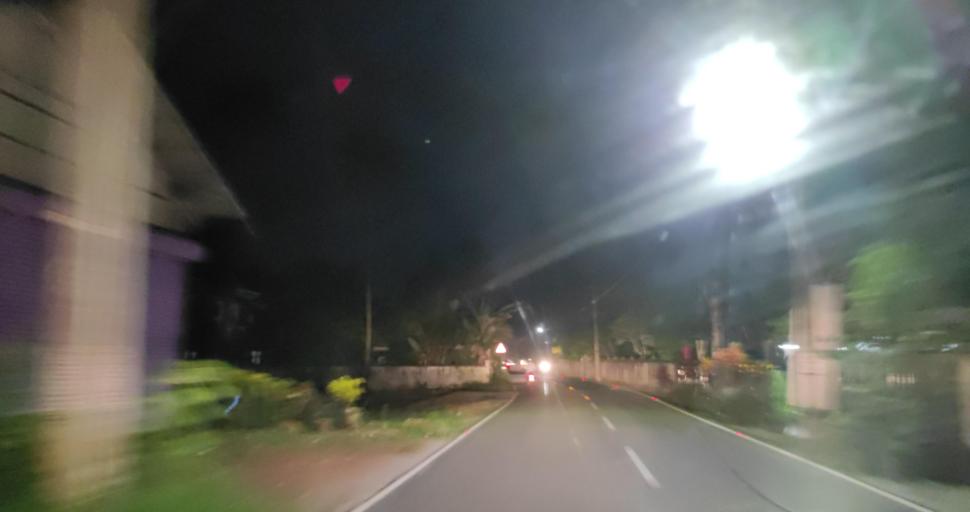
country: IN
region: Kerala
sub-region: Alappuzha
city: Vayalar
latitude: 9.6808
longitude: 76.3222
